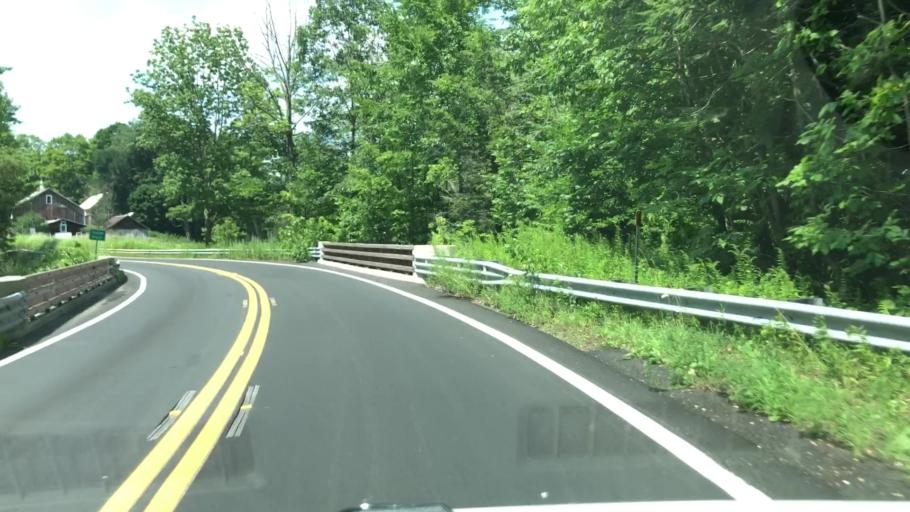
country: US
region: Massachusetts
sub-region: Franklin County
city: Ashfield
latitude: 42.5092
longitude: -72.7716
